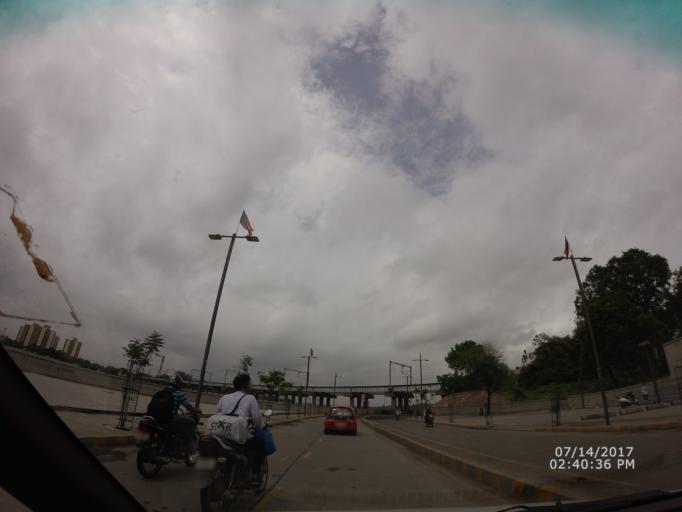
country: IN
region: Gujarat
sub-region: Ahmadabad
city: Ahmedabad
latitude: 23.0612
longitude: 72.5886
